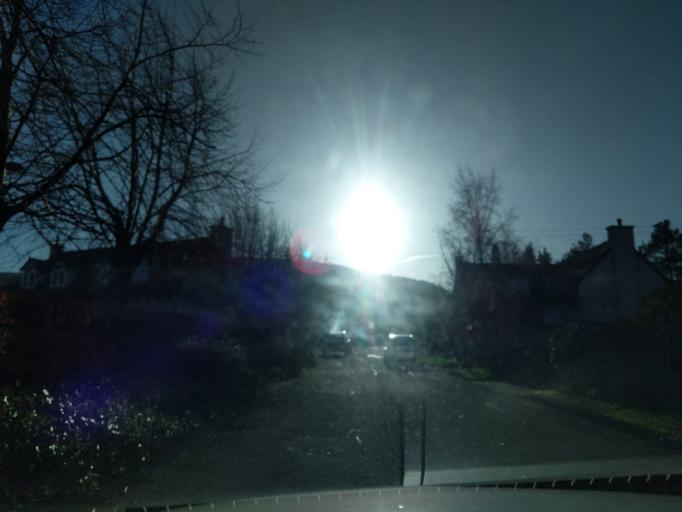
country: GB
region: Scotland
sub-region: Edinburgh
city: Colinton
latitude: 55.9001
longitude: -3.2636
